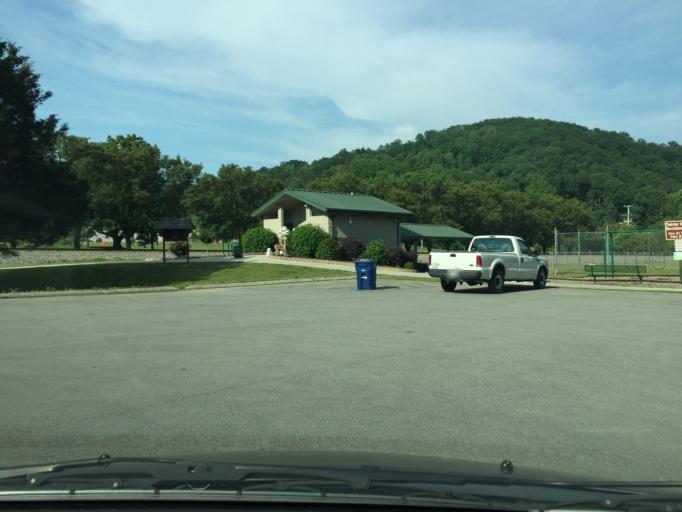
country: US
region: Tennessee
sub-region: Hamilton County
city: Collegedale
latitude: 35.0541
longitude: -85.0502
